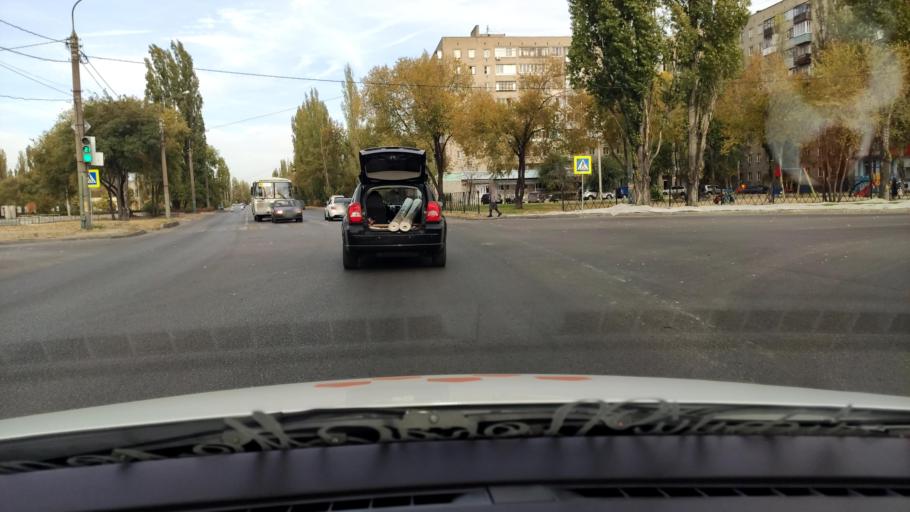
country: RU
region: Voronezj
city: Maslovka
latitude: 51.6337
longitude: 39.2632
